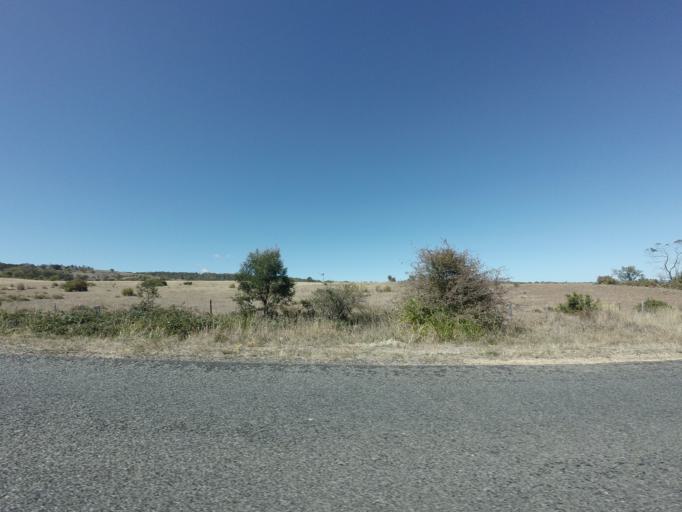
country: AU
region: Tasmania
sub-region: Break O'Day
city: St Helens
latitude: -41.9975
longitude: 148.0913
